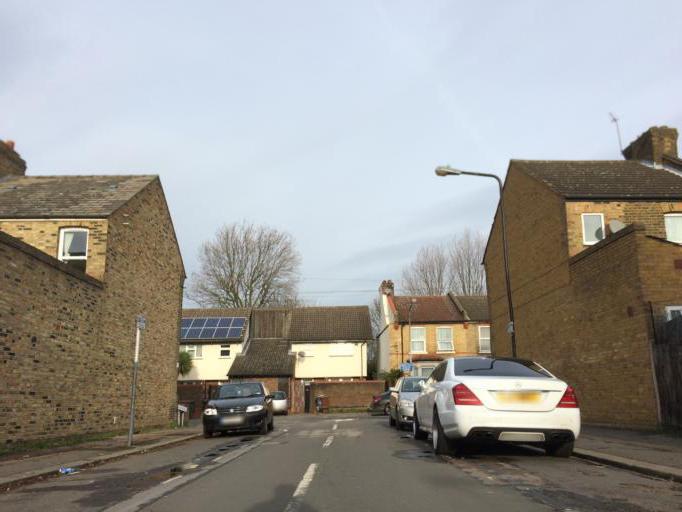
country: GB
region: England
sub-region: Greater London
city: Walthamstow
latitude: 51.5814
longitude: -0.0257
